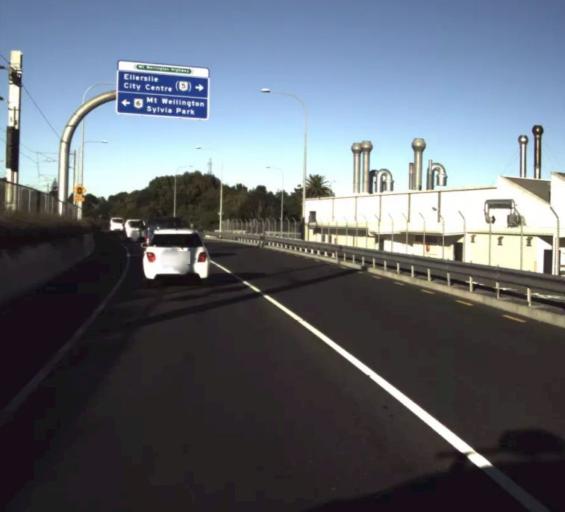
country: NZ
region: Auckland
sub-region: Auckland
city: Tamaki
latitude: -36.9026
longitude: 174.8441
